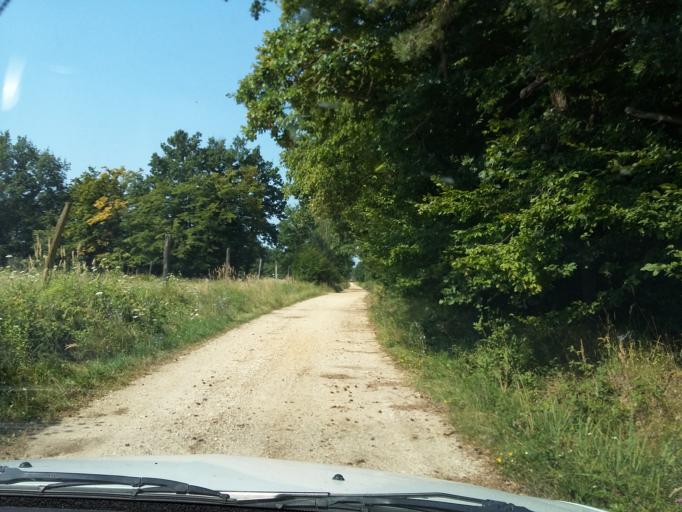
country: SI
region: Hodos-Hodos
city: Hodos
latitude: 46.8597
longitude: 16.3413
